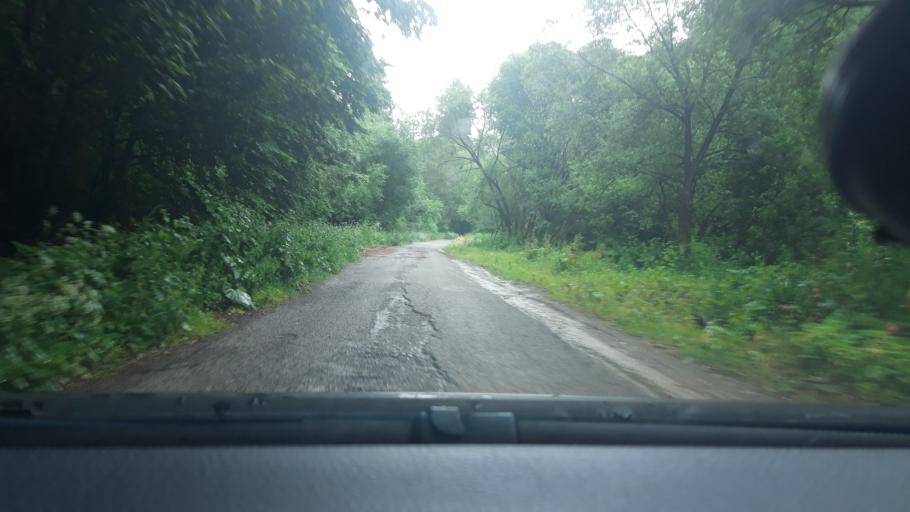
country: SK
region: Zilinsky
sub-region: Okres Martin
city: Martin
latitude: 49.0126
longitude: 19.0228
